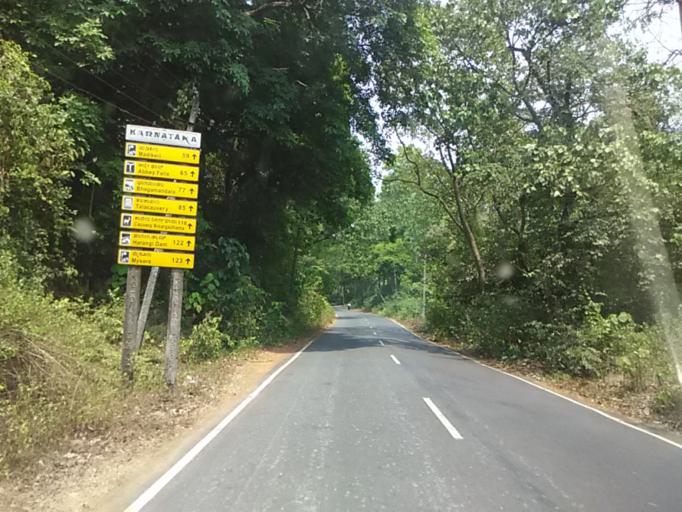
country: IN
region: Karnataka
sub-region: Kodagu
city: Virarajendrapet
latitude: 12.0733
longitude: 75.7254
